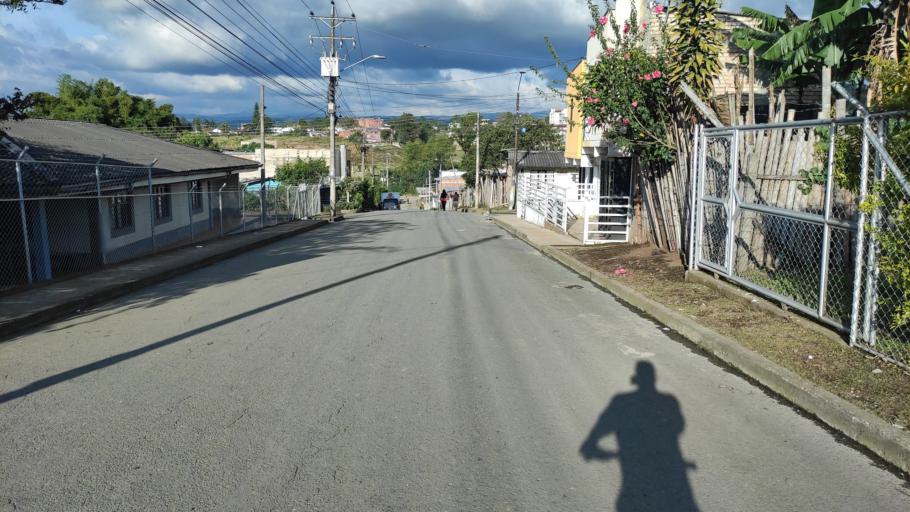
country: CO
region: Cauca
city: Popayan
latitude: 2.4897
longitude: -76.5674
